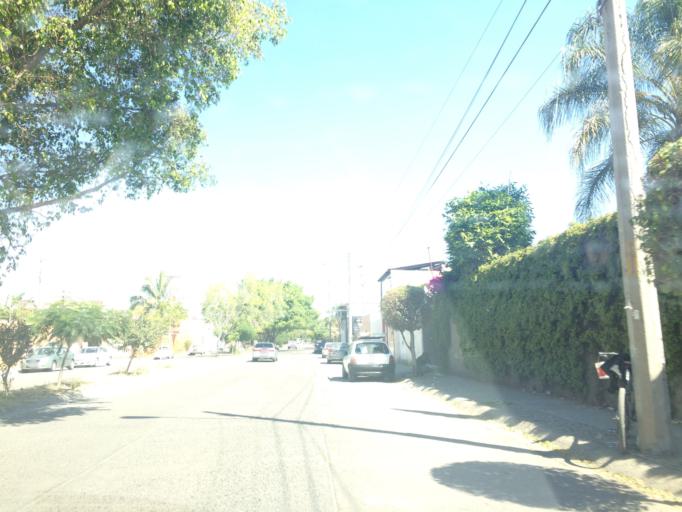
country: MX
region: Guanajuato
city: Leon
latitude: 21.1018
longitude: -101.6700
